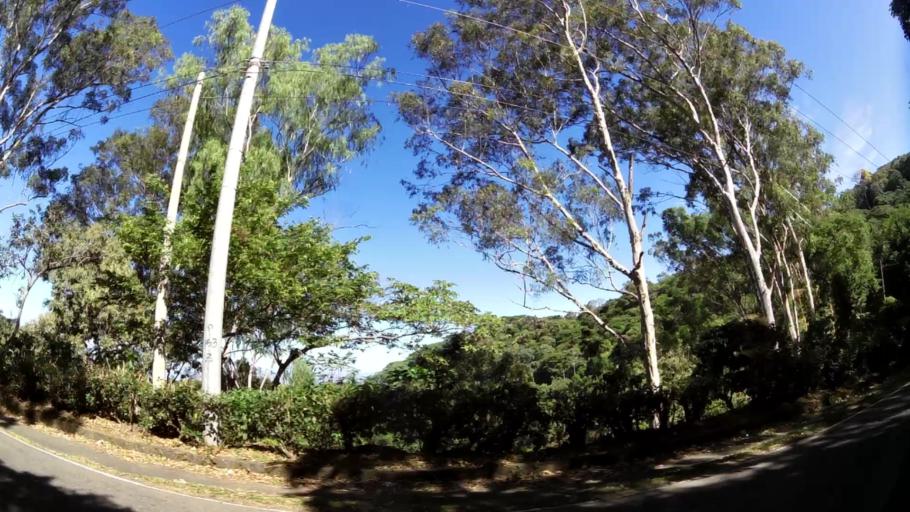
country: SV
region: Ahuachapan
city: Concepcion de Ataco
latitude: 13.8871
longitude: -89.8420
